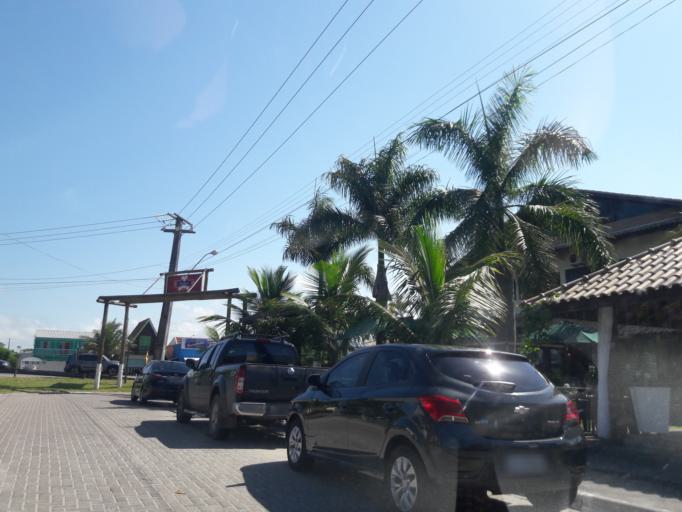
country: BR
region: Parana
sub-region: Pontal Do Parana
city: Pontal do Parana
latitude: -25.6984
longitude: -48.4736
